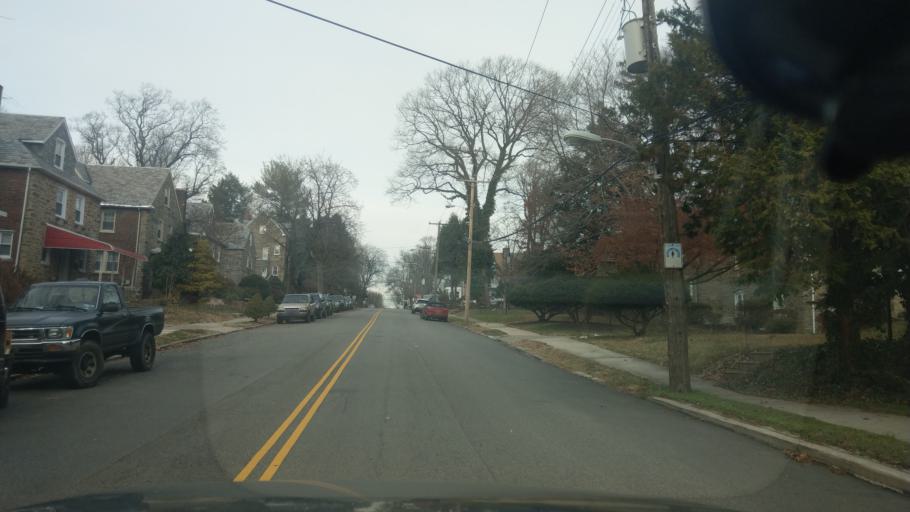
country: US
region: Pennsylvania
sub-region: Montgomery County
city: Wyncote
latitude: 40.0473
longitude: -75.1391
